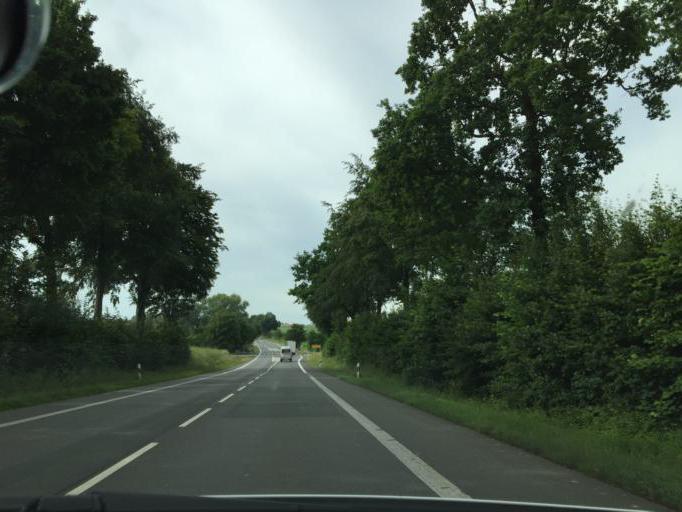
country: DE
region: North Rhine-Westphalia
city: Warburg
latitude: 51.5544
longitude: 9.1326
